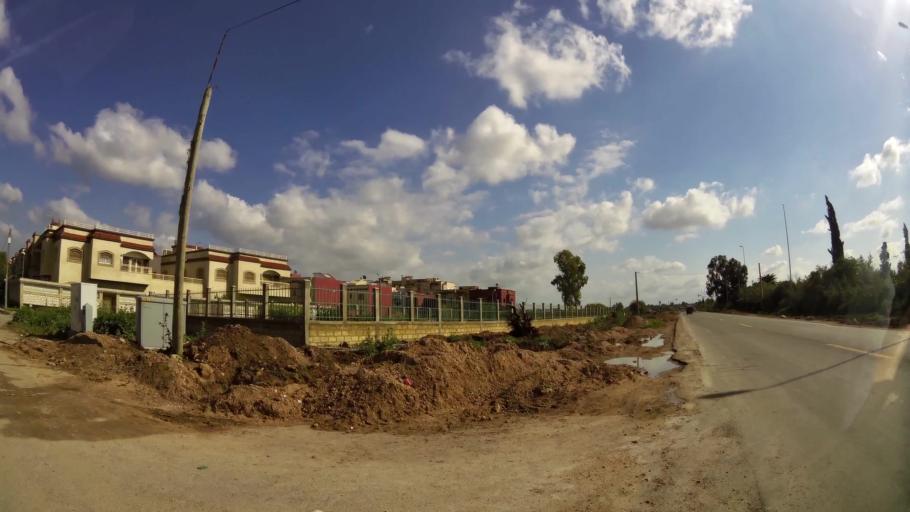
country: MA
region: Grand Casablanca
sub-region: Mediouna
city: Mediouna
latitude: 33.3852
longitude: -7.5380
